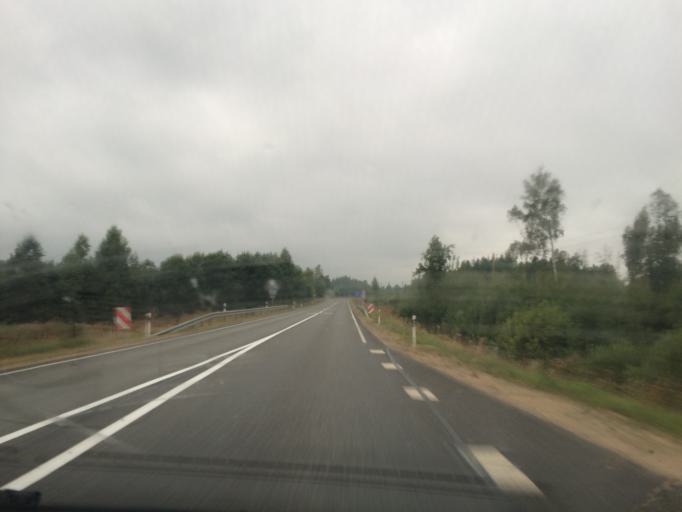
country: LV
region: Livani
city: Livani
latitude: 56.5240
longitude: 26.4217
